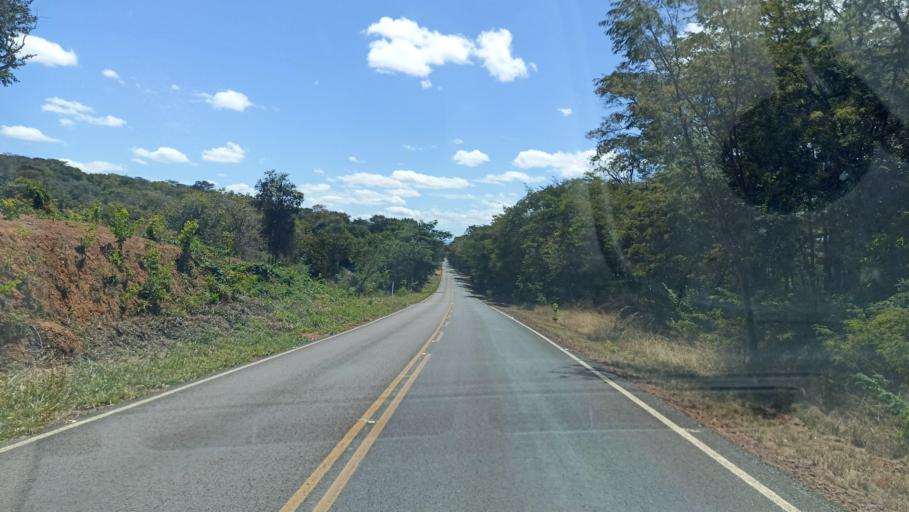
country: BR
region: Bahia
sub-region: Andarai
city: Vera Cruz
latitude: -12.7848
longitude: -41.3286
